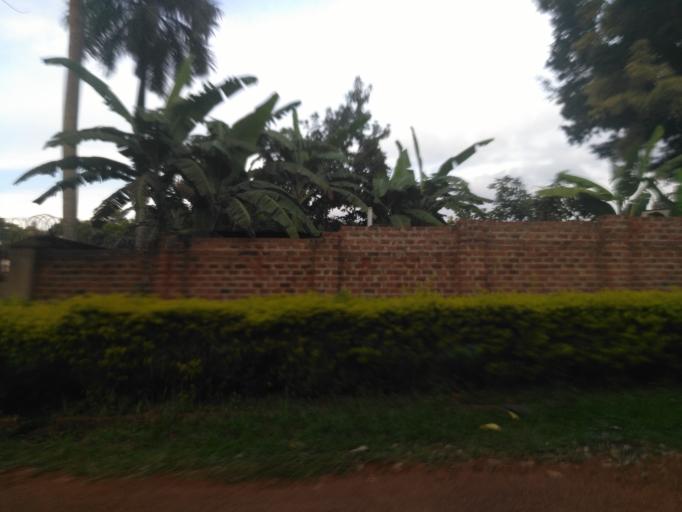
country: UG
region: Eastern Region
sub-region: Jinja District
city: Jinja
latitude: 0.4391
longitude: 33.1990
